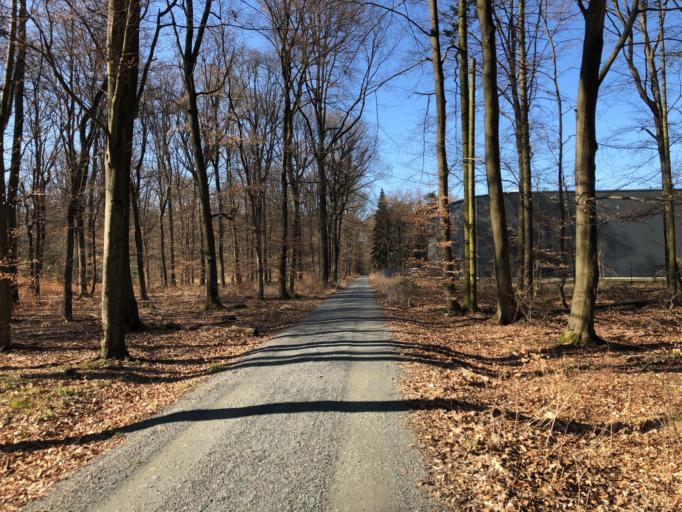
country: DE
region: Hesse
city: Langen
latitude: 50.0185
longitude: 8.6570
